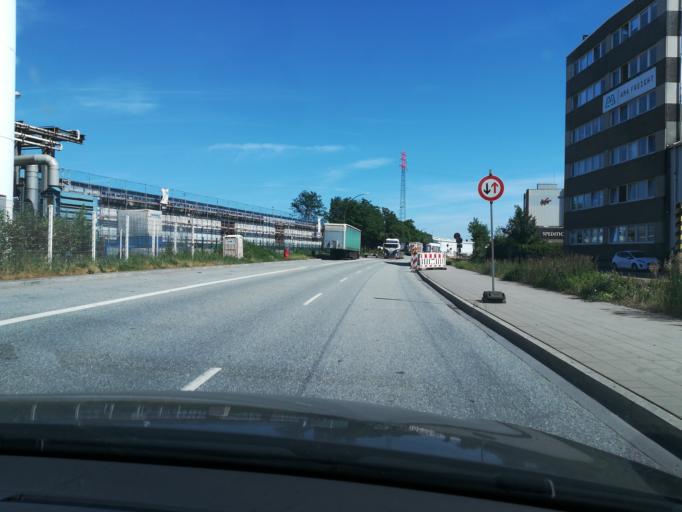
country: DE
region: Hamburg
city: Rothenburgsort
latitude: 53.5195
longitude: 10.0498
